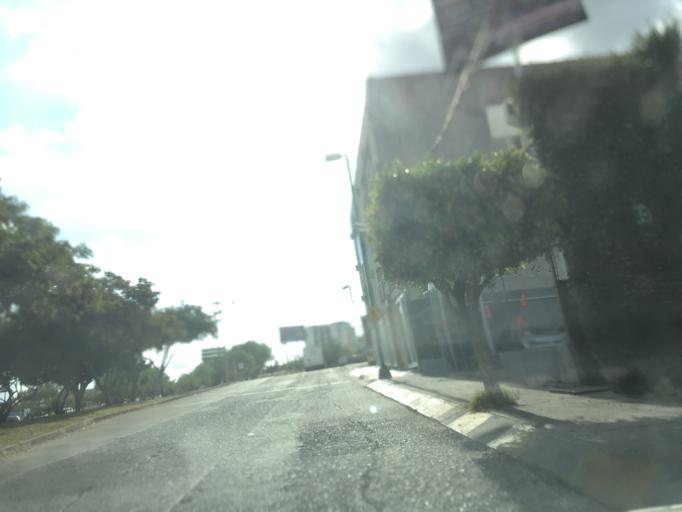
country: MX
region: Guanajuato
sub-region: Leon
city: La Ermita
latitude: 21.1494
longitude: -101.7064
